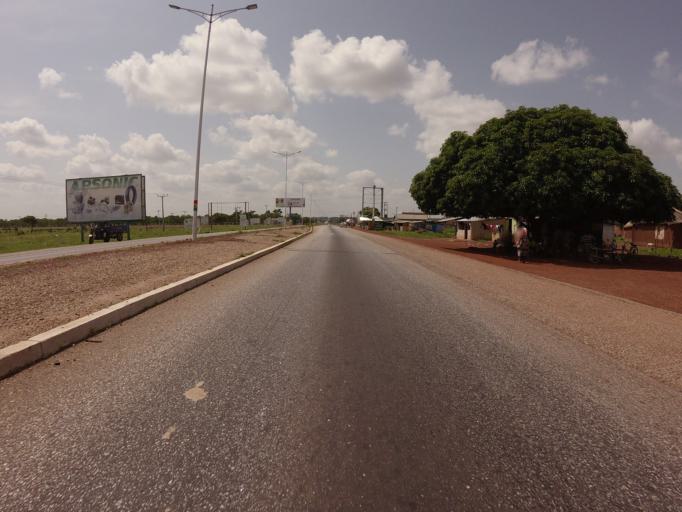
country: GH
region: Northern
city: Savelugu
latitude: 9.5511
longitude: -0.8376
